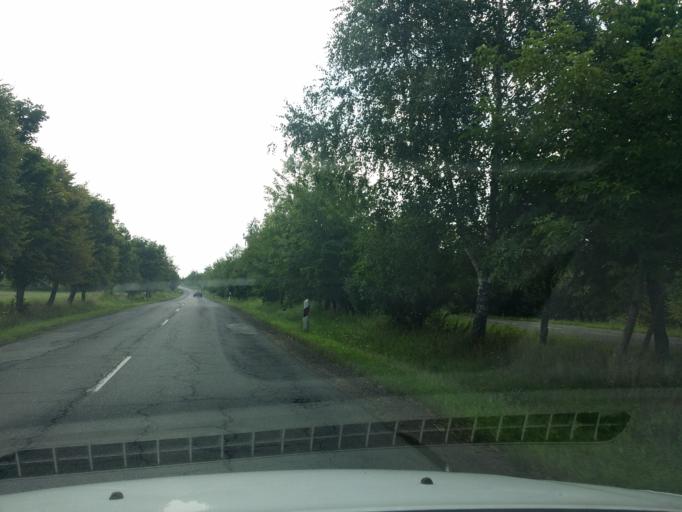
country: HU
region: Borsod-Abauj-Zemplen
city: Satoraljaujhely
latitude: 48.4682
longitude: 21.5809
